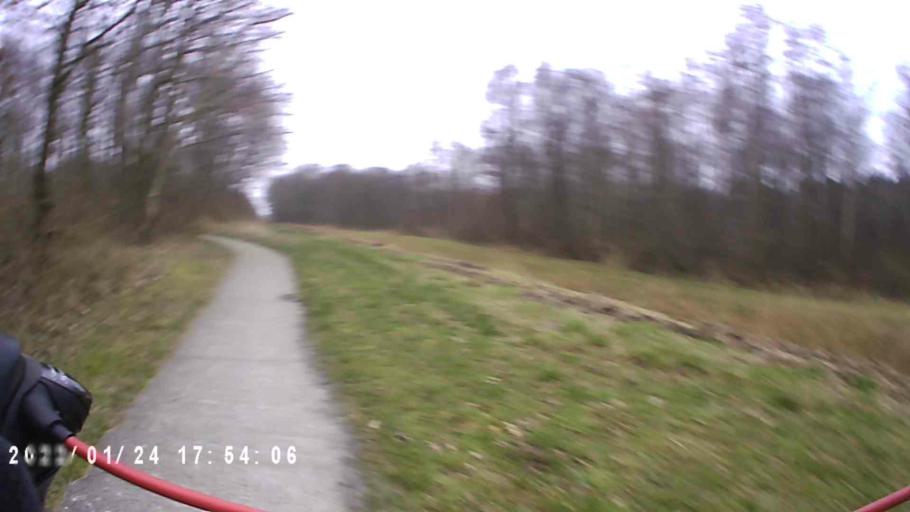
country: NL
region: Friesland
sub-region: Gemeente Dongeradeel
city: Anjum
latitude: 53.4044
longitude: 6.2328
